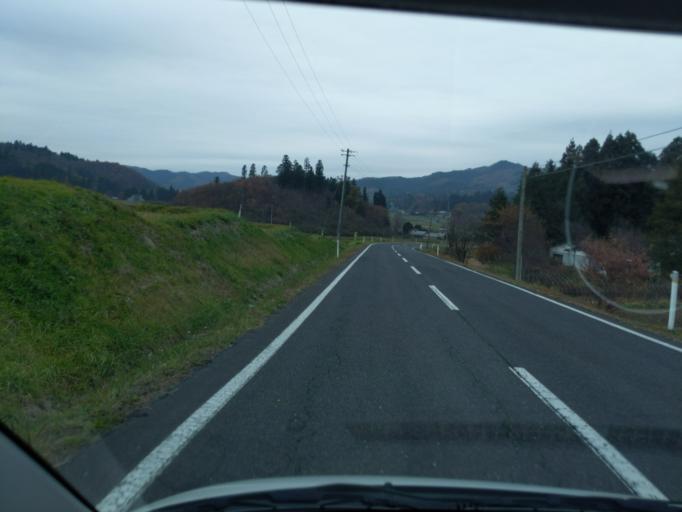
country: JP
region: Iwate
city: Kitakami
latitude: 39.2550
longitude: 141.2065
